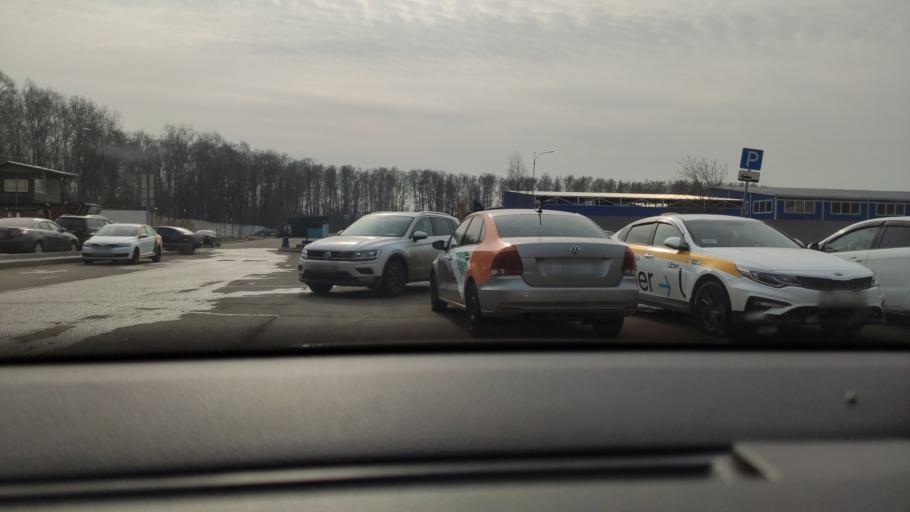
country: RU
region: Moskovskaya
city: Razvilka
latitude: 55.5994
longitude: 37.7385
